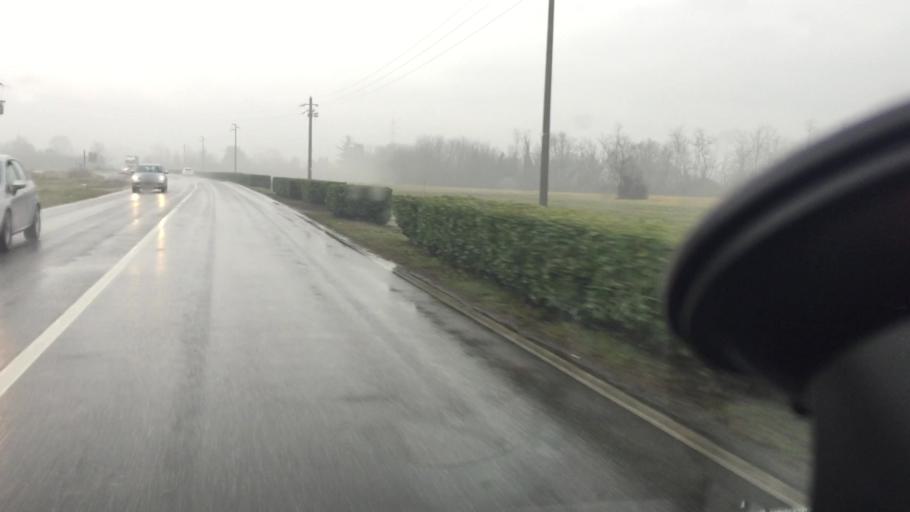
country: IT
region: Lombardy
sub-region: Citta metropolitana di Milano
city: Trezzo sull'Adda
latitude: 45.5925
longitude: 9.5223
